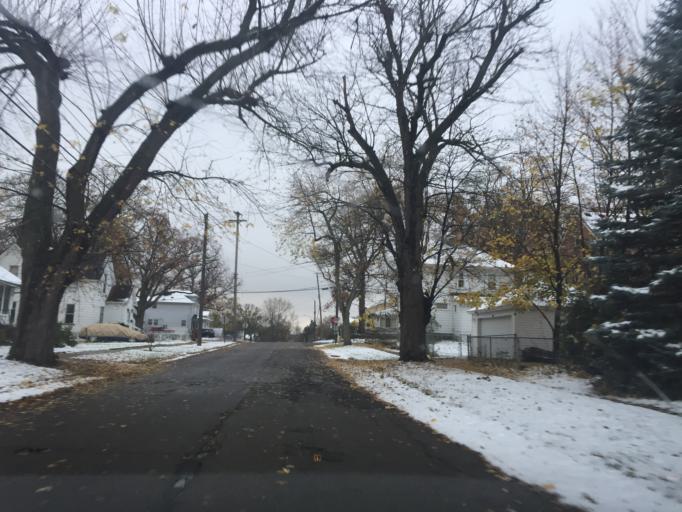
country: US
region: Michigan
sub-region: Oakland County
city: Pontiac
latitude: 42.6333
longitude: -83.2794
